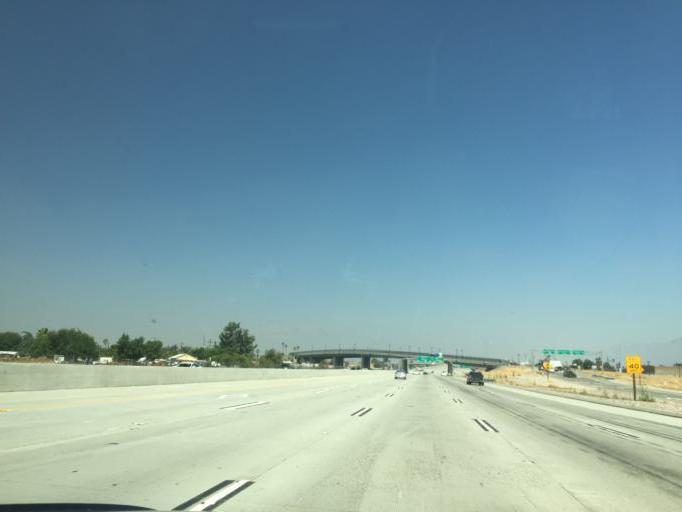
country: US
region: California
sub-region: San Bernardino County
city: San Bernardino
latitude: 34.1340
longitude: -117.3096
